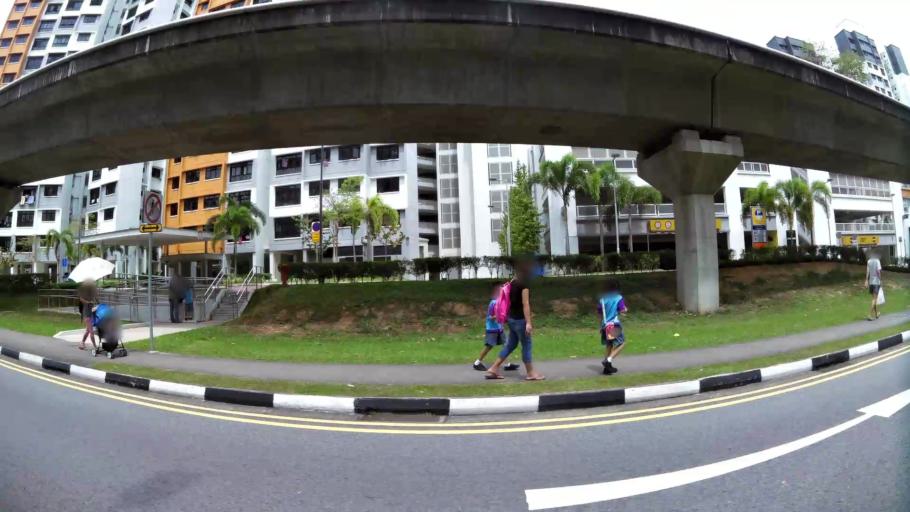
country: MY
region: Johor
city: Johor Bahru
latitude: 1.3880
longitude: 103.7690
